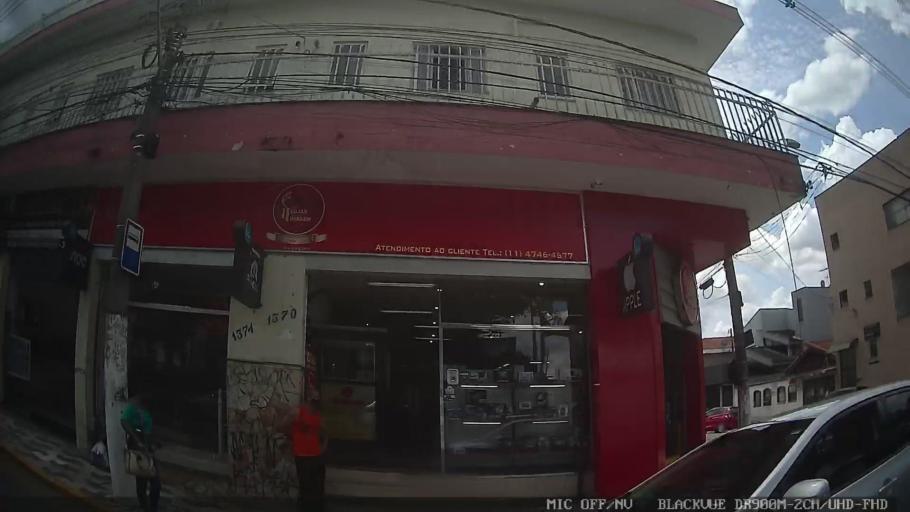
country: BR
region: Sao Paulo
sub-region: Suzano
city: Suzano
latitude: -23.5457
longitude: -46.3137
